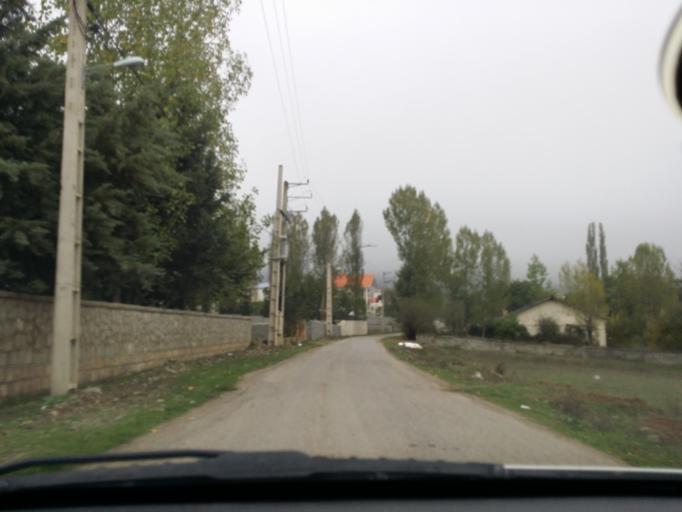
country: IR
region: Mazandaran
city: Chalus
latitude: 36.5134
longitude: 51.2262
